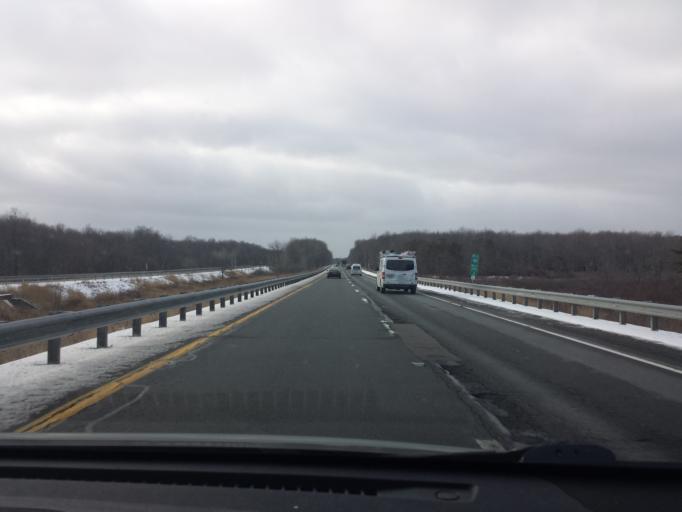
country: US
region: Pennsylvania
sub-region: Monroe County
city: Pocono Pines
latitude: 41.0726
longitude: -75.4536
